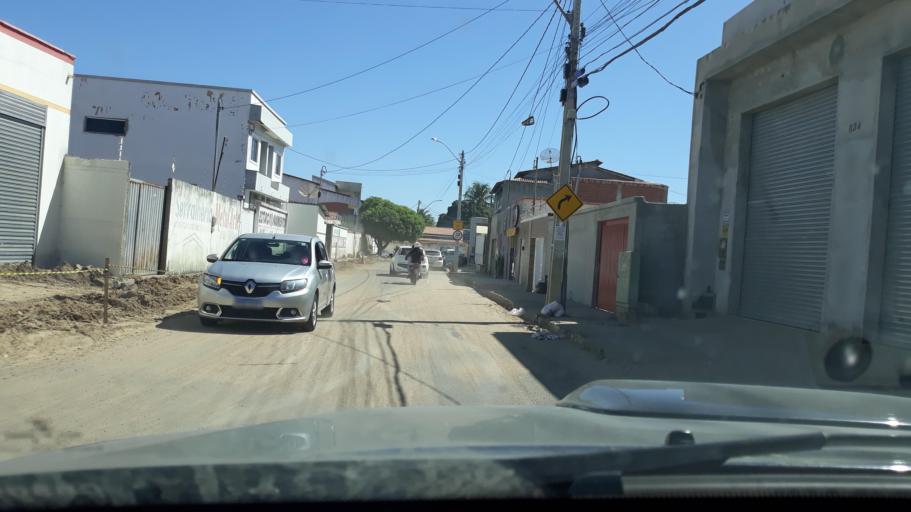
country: BR
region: Bahia
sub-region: Guanambi
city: Guanambi
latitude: -14.2252
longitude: -42.7886
